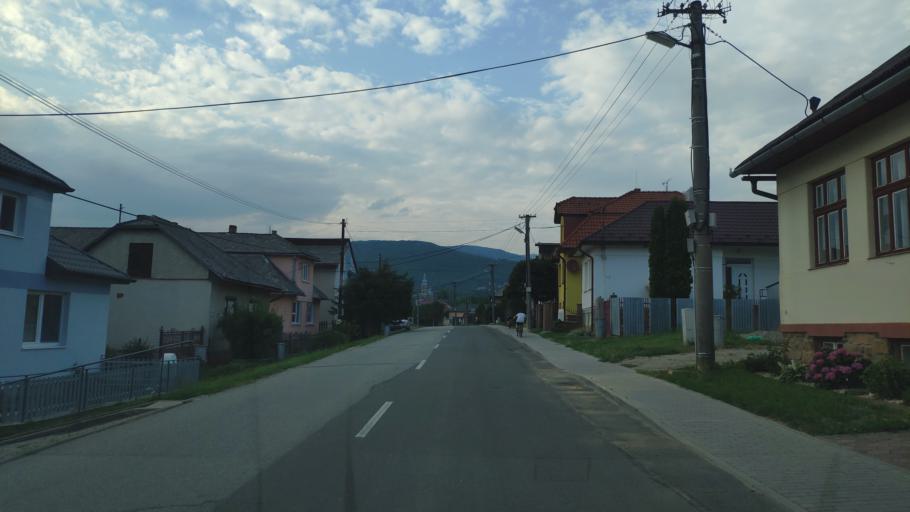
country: SK
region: Kosicky
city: Medzev
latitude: 48.7050
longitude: 20.9752
